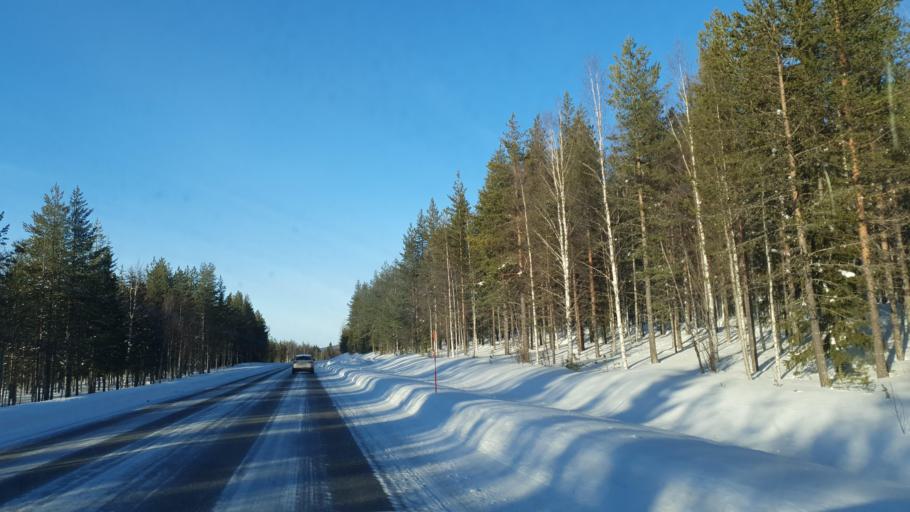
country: FI
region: Lapland
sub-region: Torniolaakso
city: Pello
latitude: 66.9918
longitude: 24.0479
